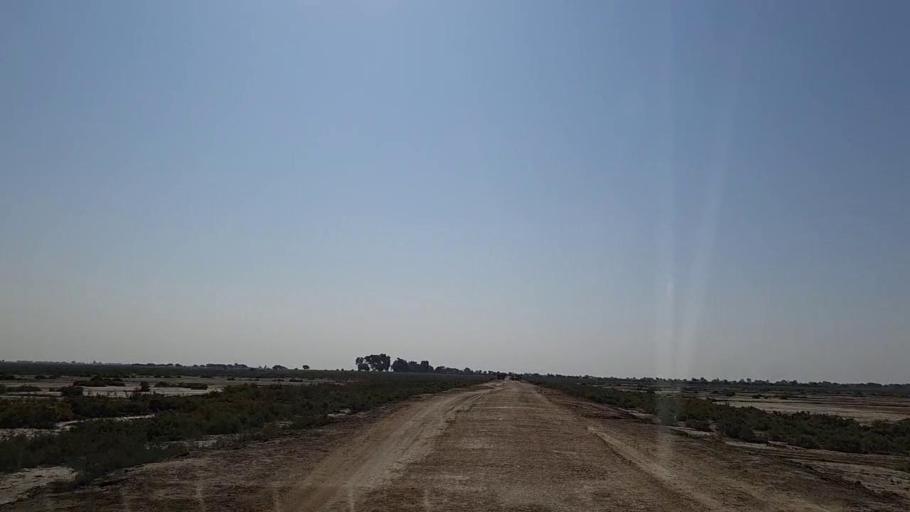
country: PK
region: Sindh
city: Chuhar Jamali
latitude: 24.5044
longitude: 68.0982
